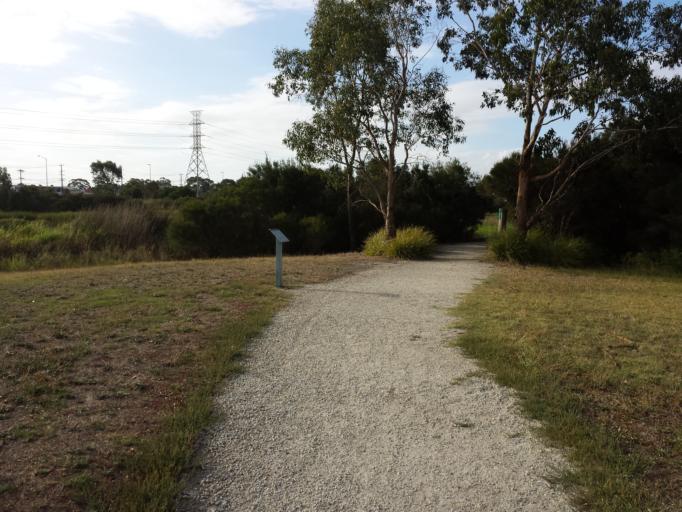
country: AU
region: Victoria
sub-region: Monash
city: Oakleigh South
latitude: -37.9416
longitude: 145.0810
